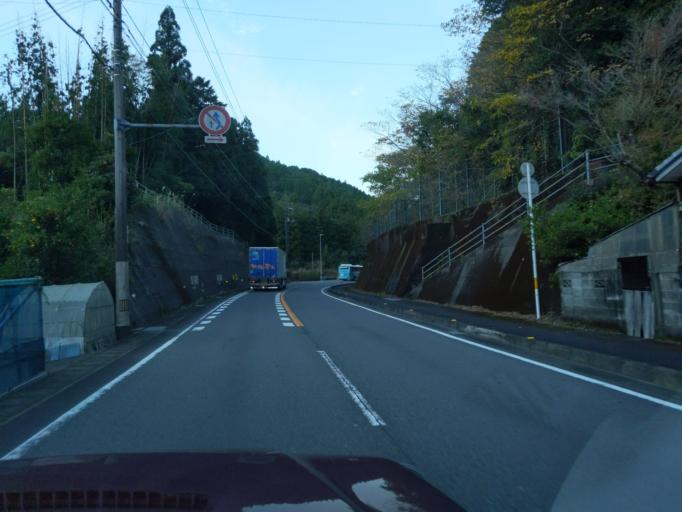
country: JP
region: Tokushima
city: Anan
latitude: 33.7129
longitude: 134.4804
